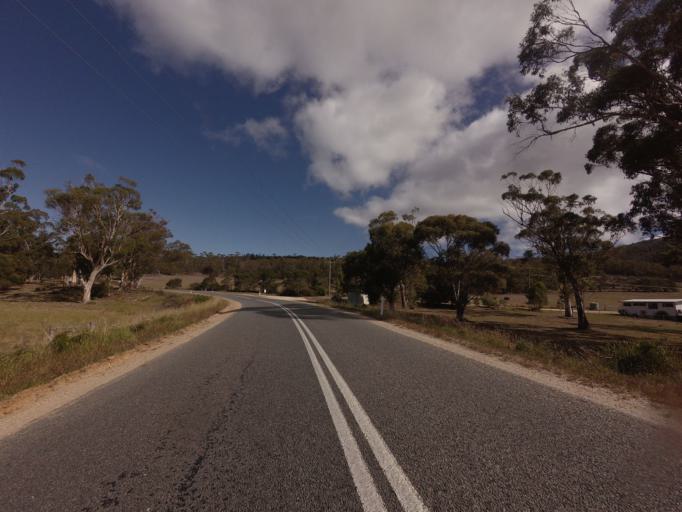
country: AU
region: Tasmania
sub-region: Break O'Day
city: St Helens
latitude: -41.7820
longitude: 148.2565
